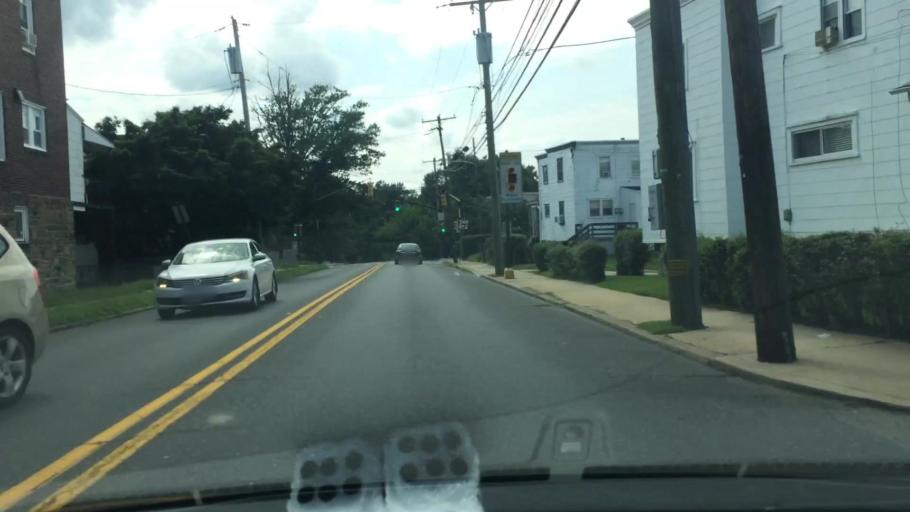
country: US
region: Pennsylvania
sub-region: Delaware County
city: Yeadon
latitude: 39.9275
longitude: -75.2500
